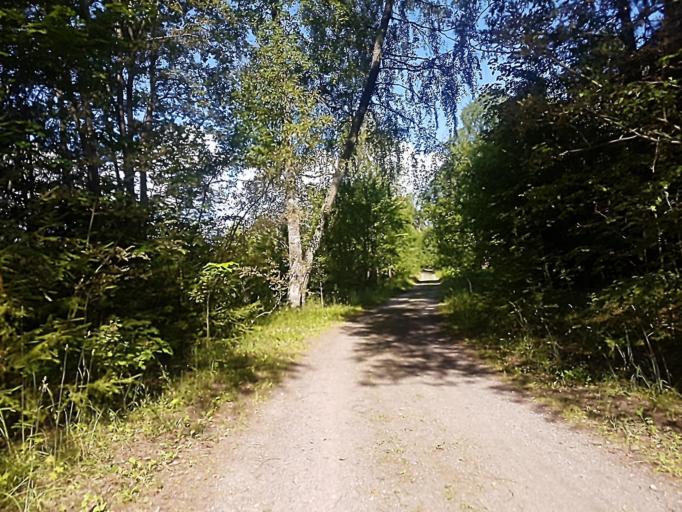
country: SE
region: Soedermanland
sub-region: Gnesta Kommun
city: Gnesta
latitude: 59.0298
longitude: 17.3561
